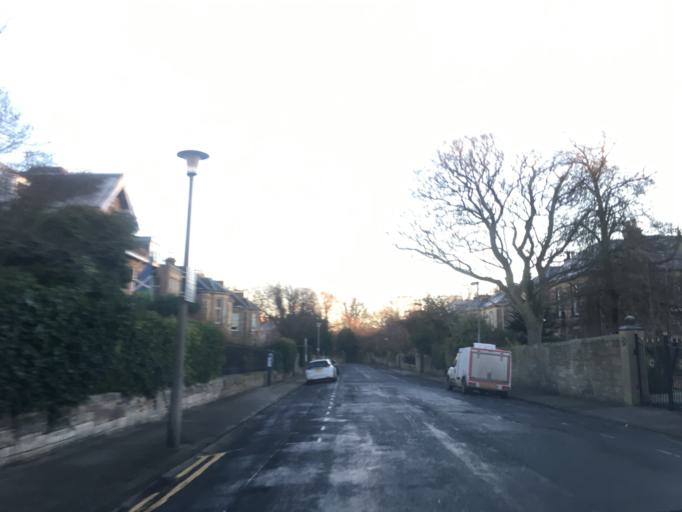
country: GB
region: Scotland
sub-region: Edinburgh
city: Edinburgh
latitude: 55.9524
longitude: -3.2311
